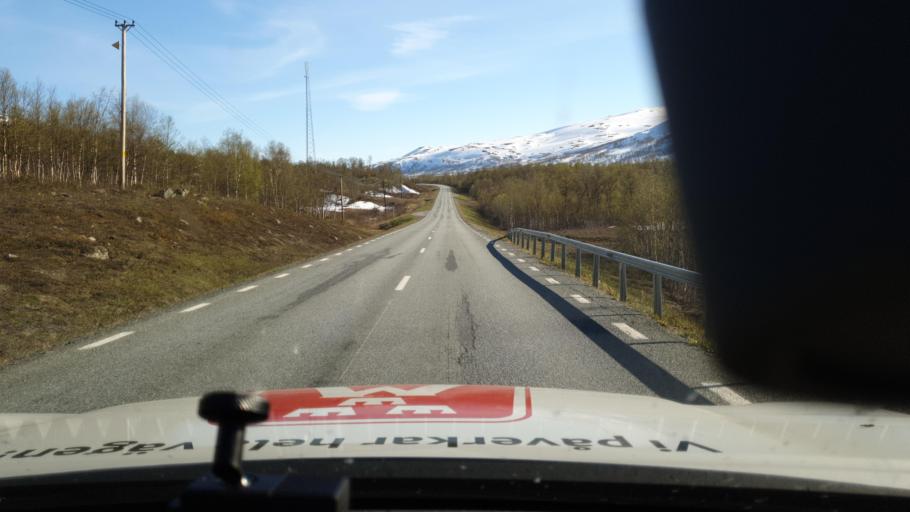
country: NO
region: Nordland
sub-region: Rana
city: Mo i Rana
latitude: 65.9150
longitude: 14.9941
